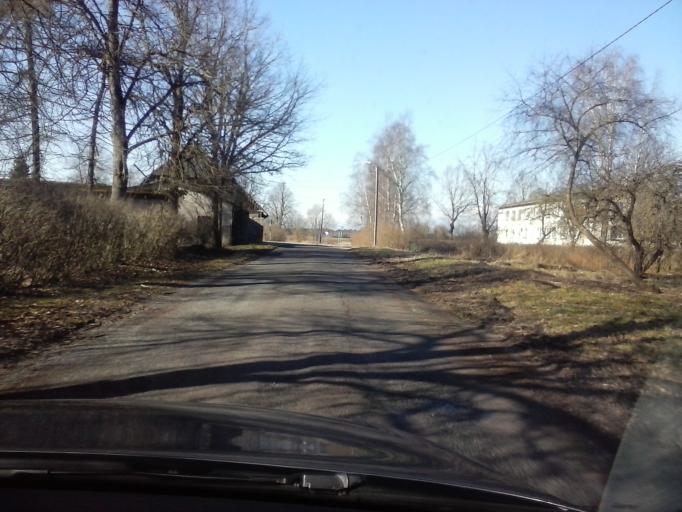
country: EE
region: Tartu
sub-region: Noo vald
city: Noo
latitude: 58.3129
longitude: 26.5478
